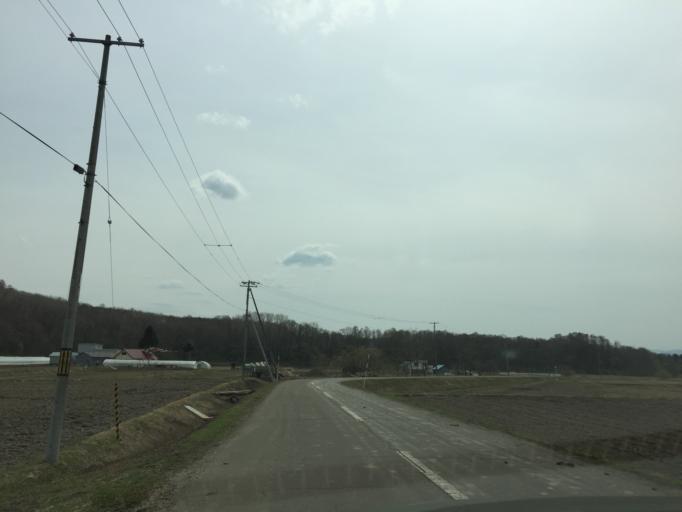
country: JP
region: Hokkaido
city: Ashibetsu
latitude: 43.6166
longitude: 142.2154
